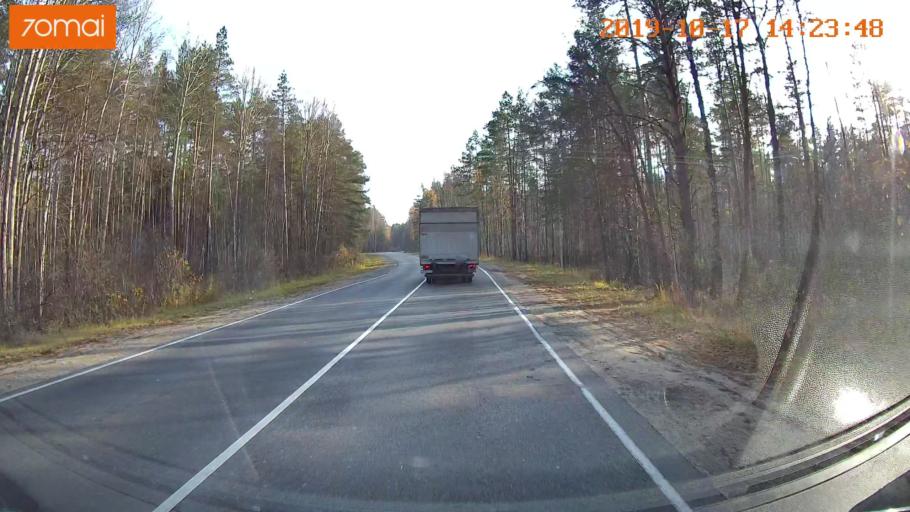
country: RU
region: Moskovskaya
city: Radovitskiy
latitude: 55.0152
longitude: 39.9626
